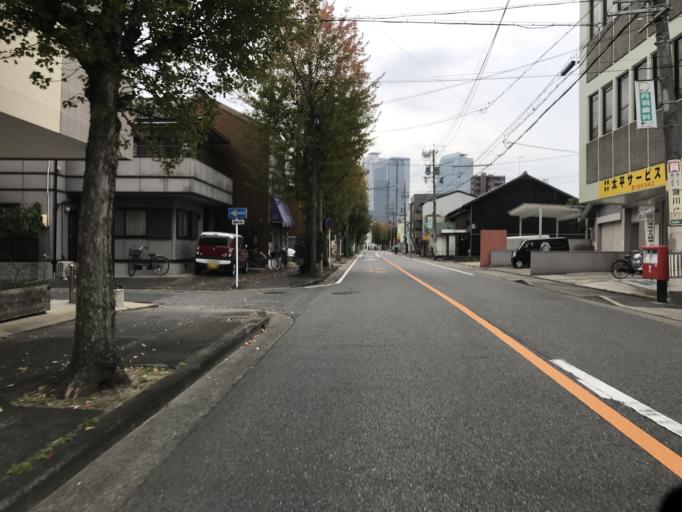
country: JP
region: Aichi
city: Nagoya-shi
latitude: 35.1849
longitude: 136.8833
